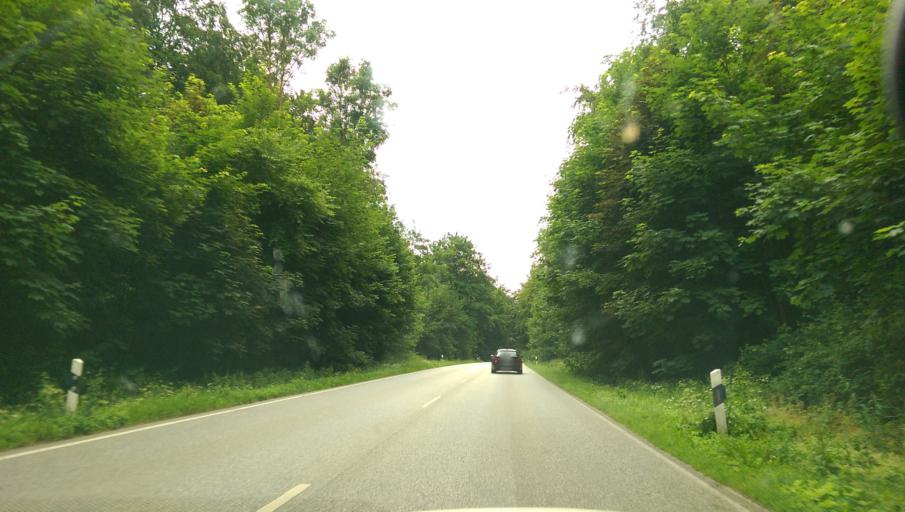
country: DE
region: Schleswig-Holstein
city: Timmendorfer Strand
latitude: 54.0056
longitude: 10.7669
